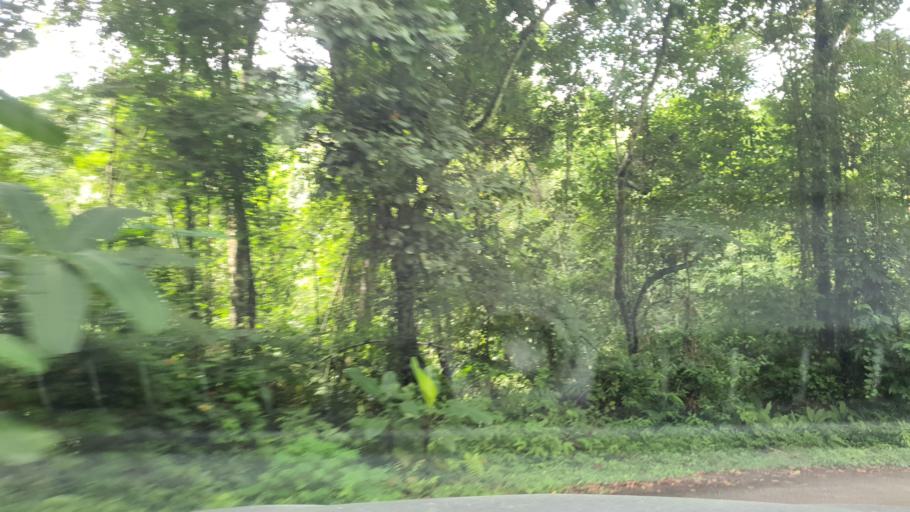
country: TH
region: Chiang Mai
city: Mae On
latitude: 18.9329
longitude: 99.3117
